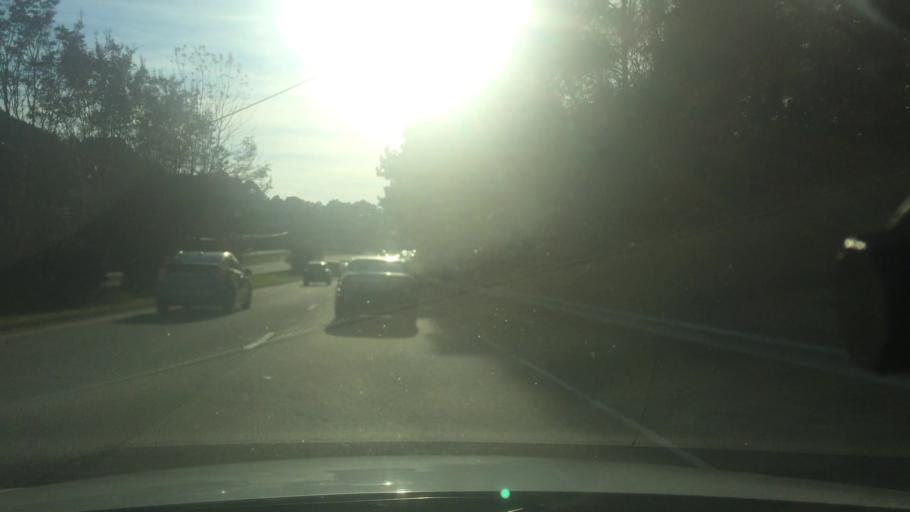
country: US
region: North Carolina
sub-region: Orange County
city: Chapel Hill
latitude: 35.9048
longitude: -78.9978
